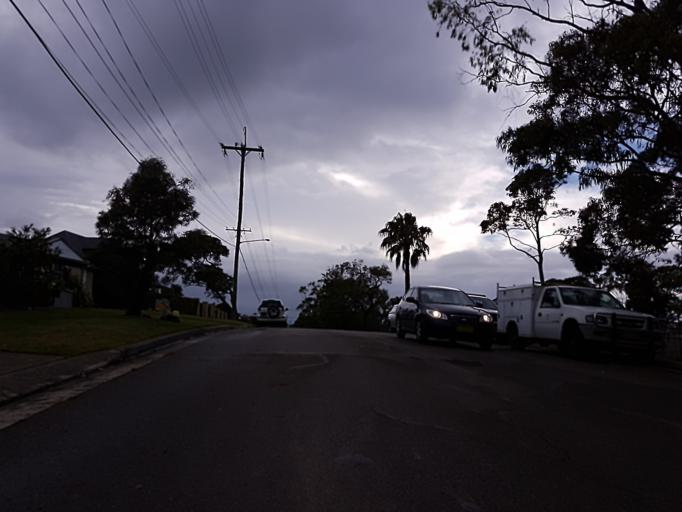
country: AU
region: New South Wales
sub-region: Warringah
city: Killarney Heights
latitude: -33.7535
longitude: 151.2264
